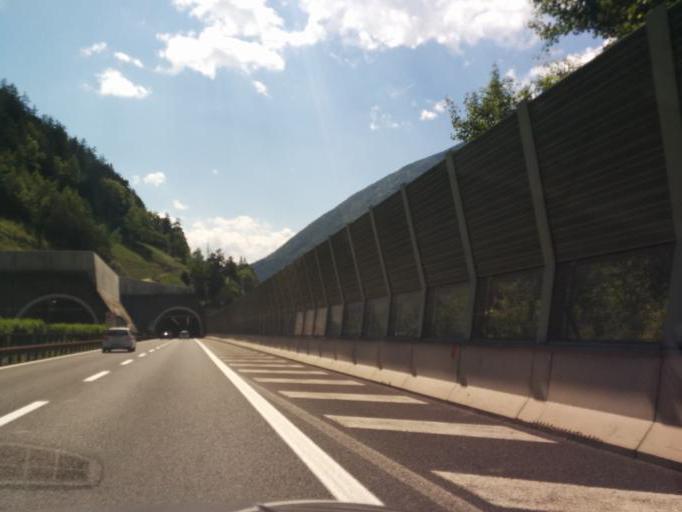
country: IT
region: Trentino-Alto Adige
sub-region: Bolzano
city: Fortezza
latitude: 46.7934
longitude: 11.6091
